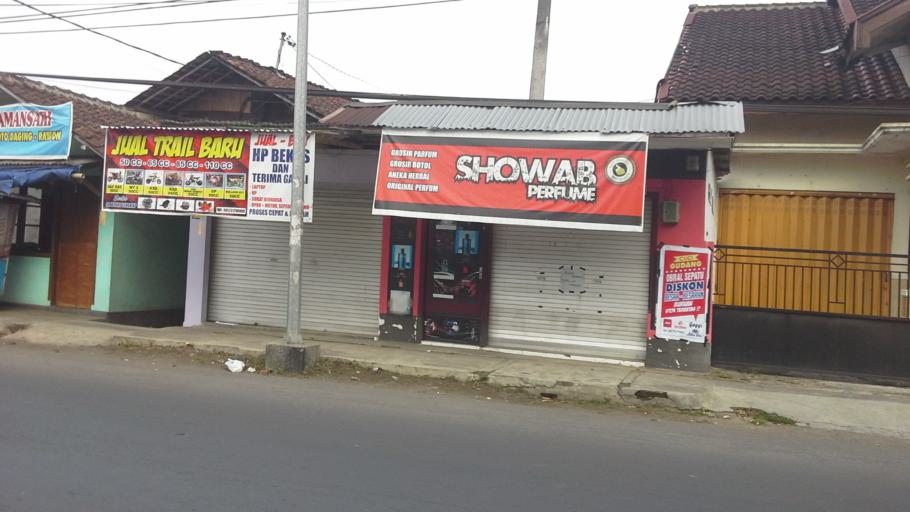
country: ID
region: East Java
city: Bondowoso
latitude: -7.9283
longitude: 113.8253
